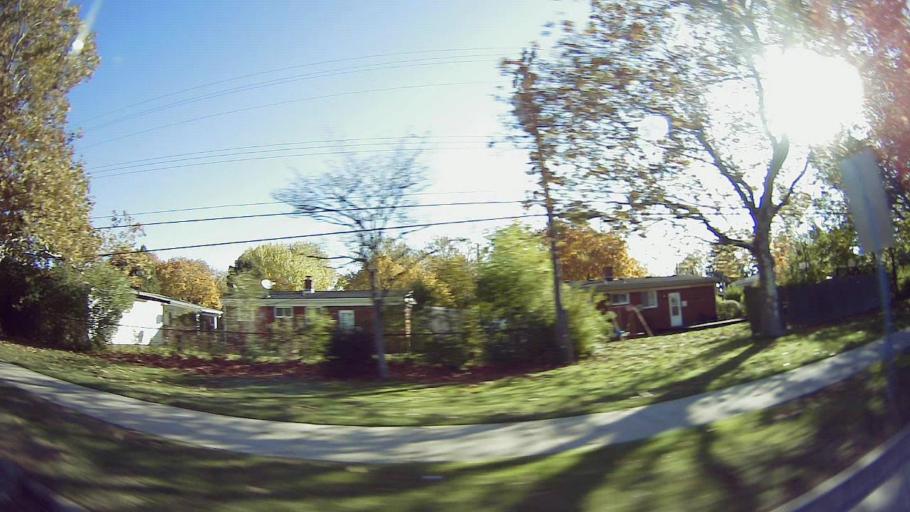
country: US
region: Michigan
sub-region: Oakland County
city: Oak Park
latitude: 42.4672
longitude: -83.2013
